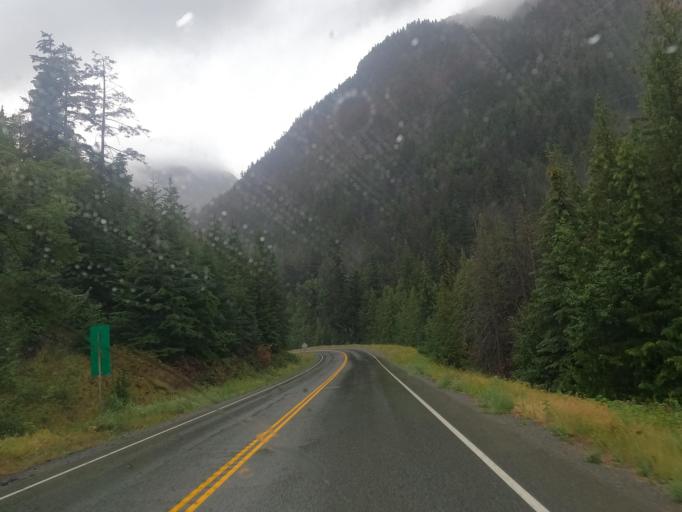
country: CA
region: British Columbia
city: Lillooet
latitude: 50.5351
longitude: -122.1412
